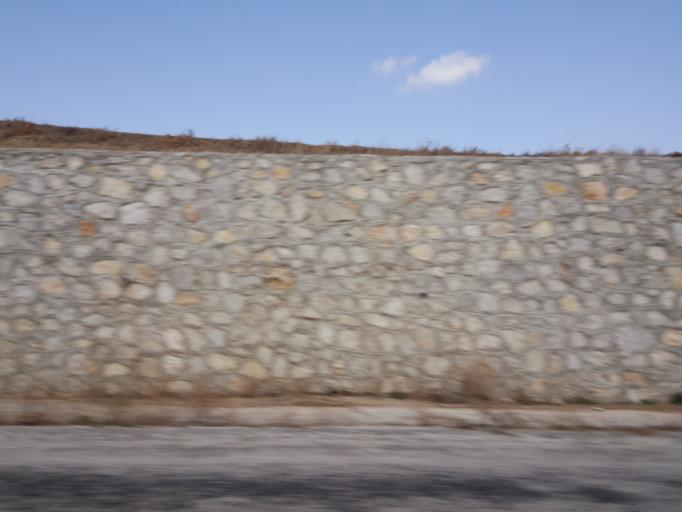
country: TR
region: Corum
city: Alaca
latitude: 40.1583
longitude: 34.7134
